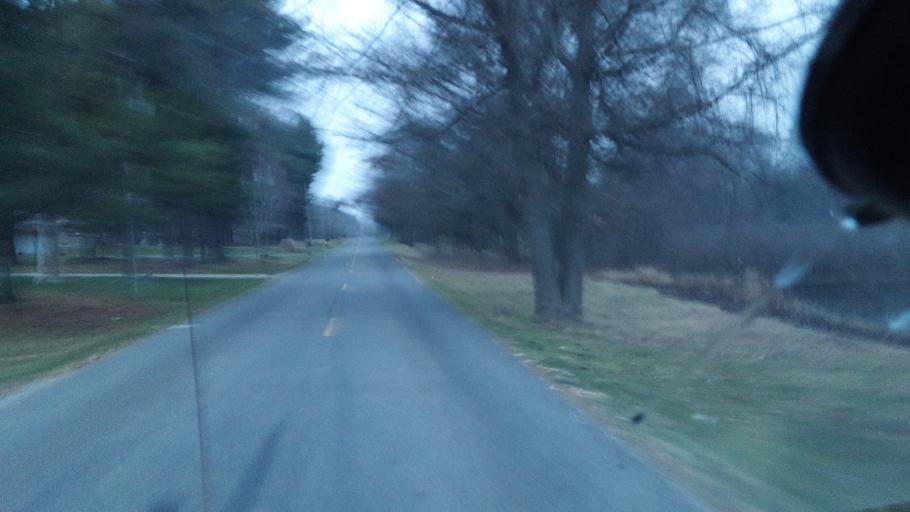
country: US
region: Indiana
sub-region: Elkhart County
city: Bristol
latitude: 41.6553
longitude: -85.7871
